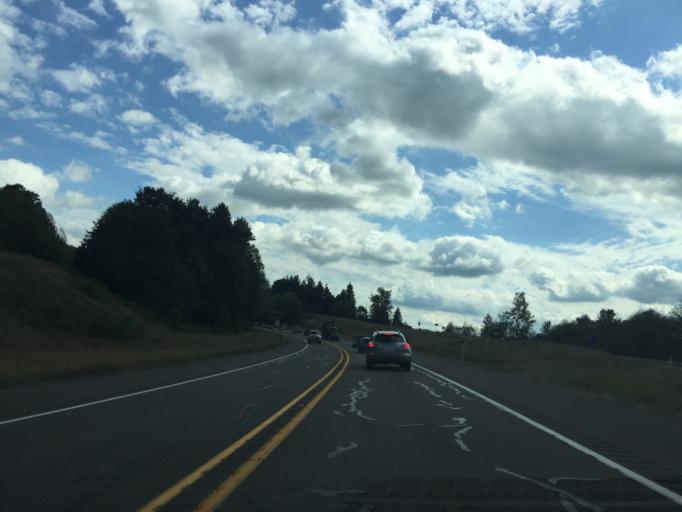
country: US
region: Washington
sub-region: Snohomish County
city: Snohomish
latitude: 47.9178
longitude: -122.0744
